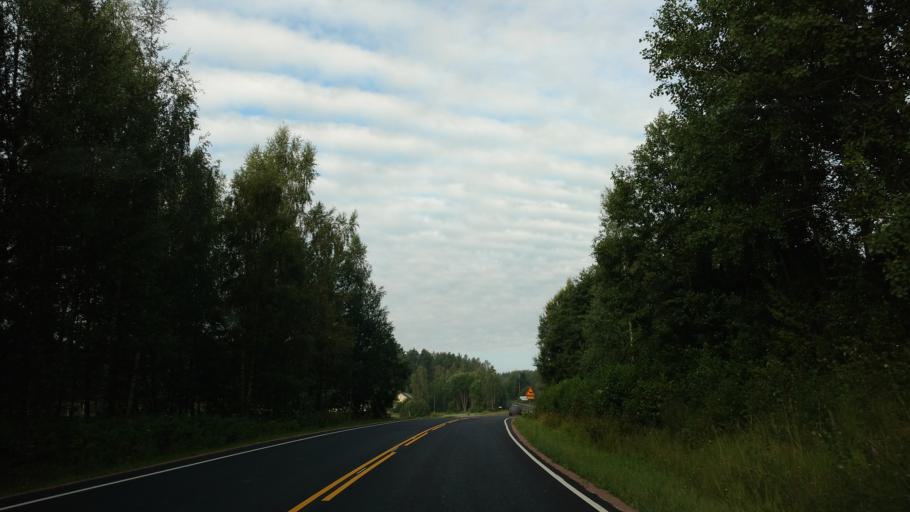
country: FI
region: Varsinais-Suomi
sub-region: Aboland-Turunmaa
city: Kimito
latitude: 60.1781
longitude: 22.8276
